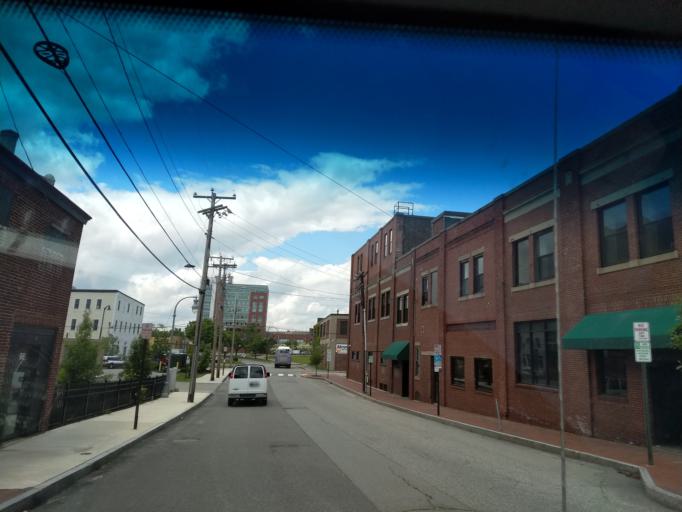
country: US
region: Maine
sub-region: Cumberland County
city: Portland
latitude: 43.6602
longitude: -70.2621
